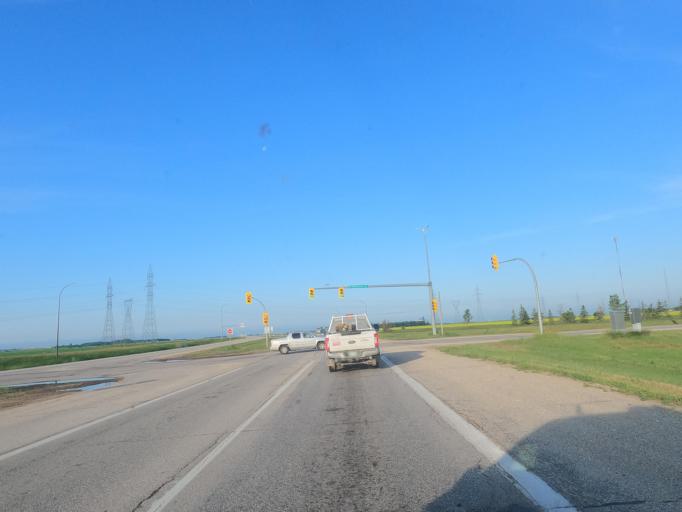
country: CA
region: Manitoba
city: Stonewall
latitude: 49.9874
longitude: -97.3096
